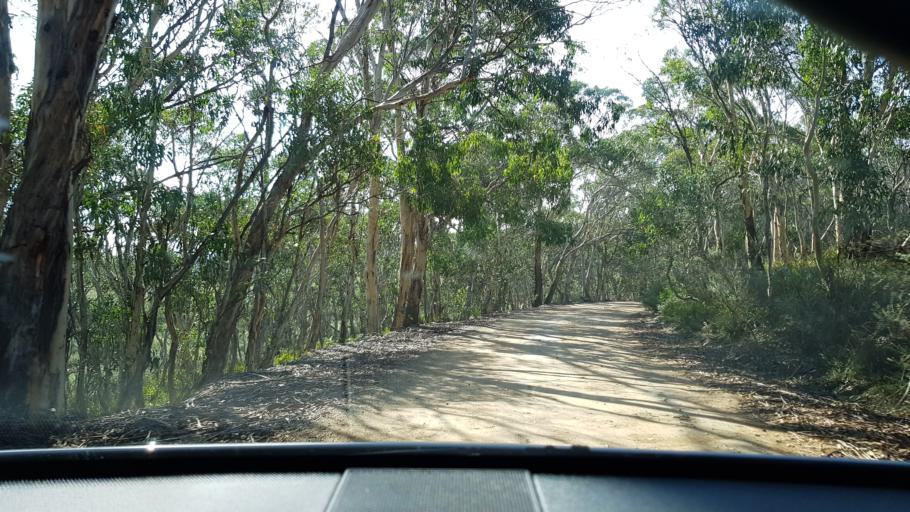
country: AU
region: New South Wales
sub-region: Oberon
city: Oberon
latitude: -33.9779
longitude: 150.0547
